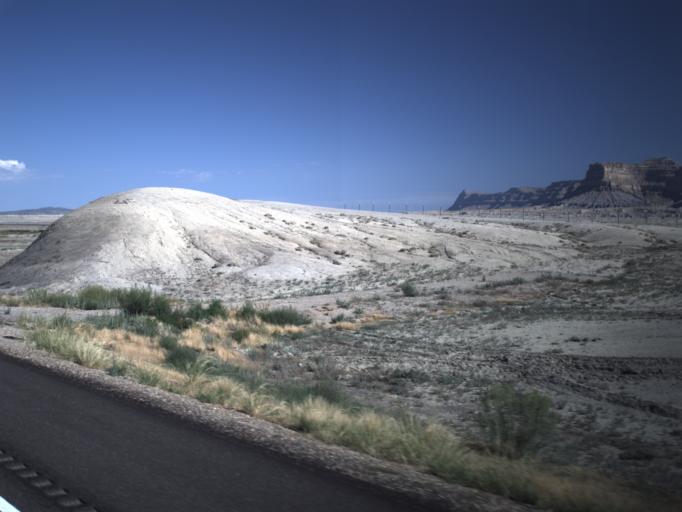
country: US
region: Utah
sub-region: Carbon County
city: East Carbon City
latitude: 38.9911
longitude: -110.2495
